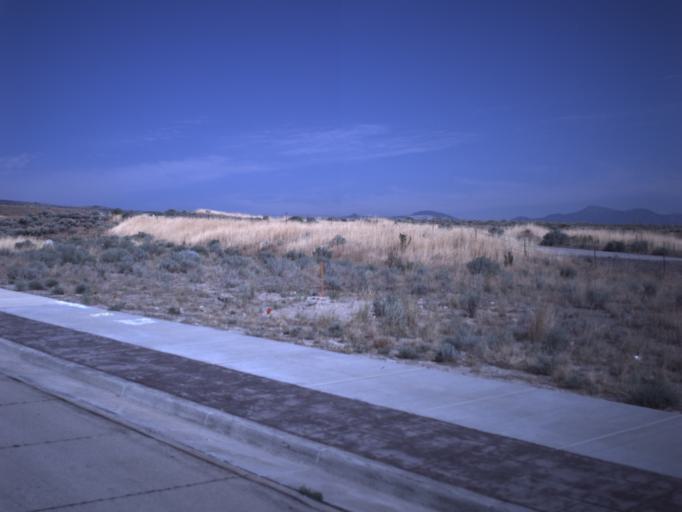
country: US
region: Utah
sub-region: Salt Lake County
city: Bluffdale
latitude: 40.4639
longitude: -111.9509
